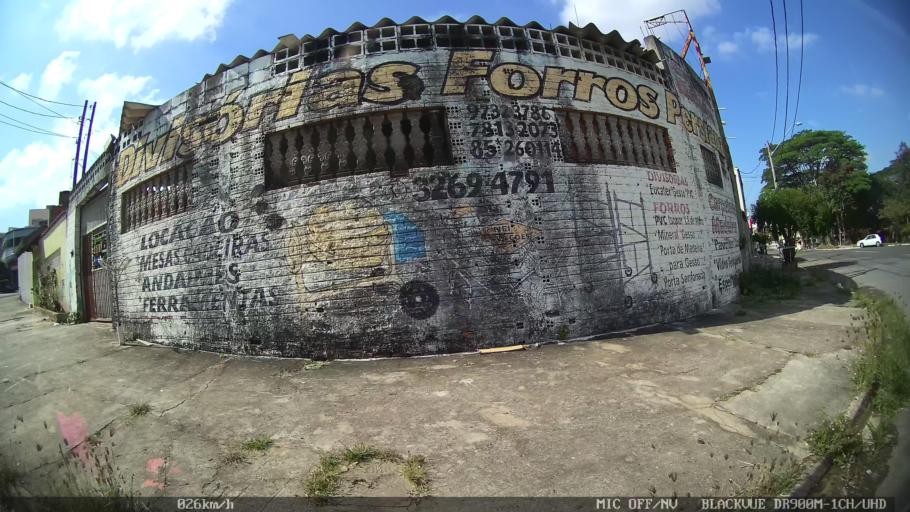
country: BR
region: Sao Paulo
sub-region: Campinas
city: Campinas
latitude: -22.9365
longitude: -47.1226
